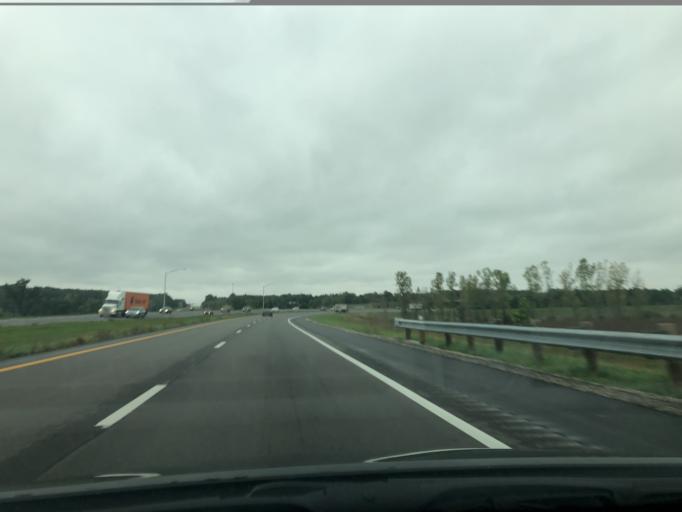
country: US
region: Ohio
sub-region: Union County
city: Marysville
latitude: 40.2421
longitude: -83.3986
